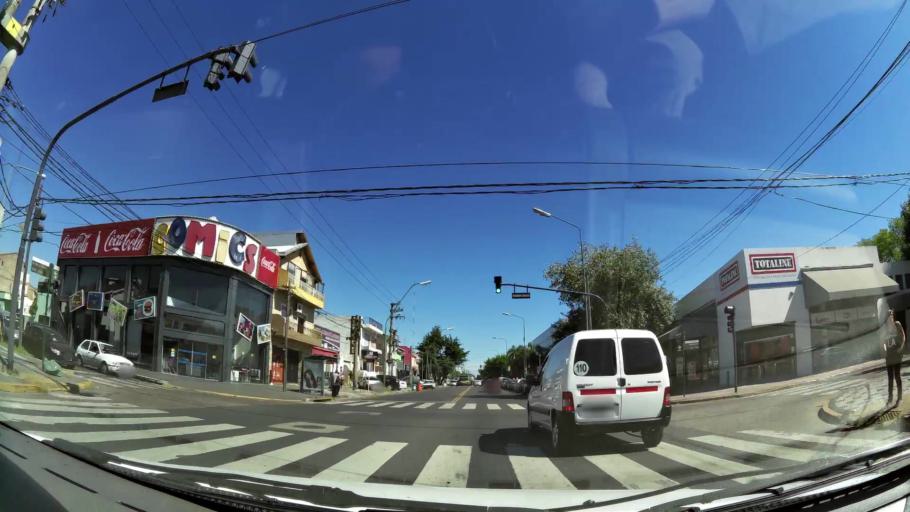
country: AR
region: Buenos Aires
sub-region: Partido de Vicente Lopez
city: Olivos
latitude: -34.5259
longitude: -58.5192
